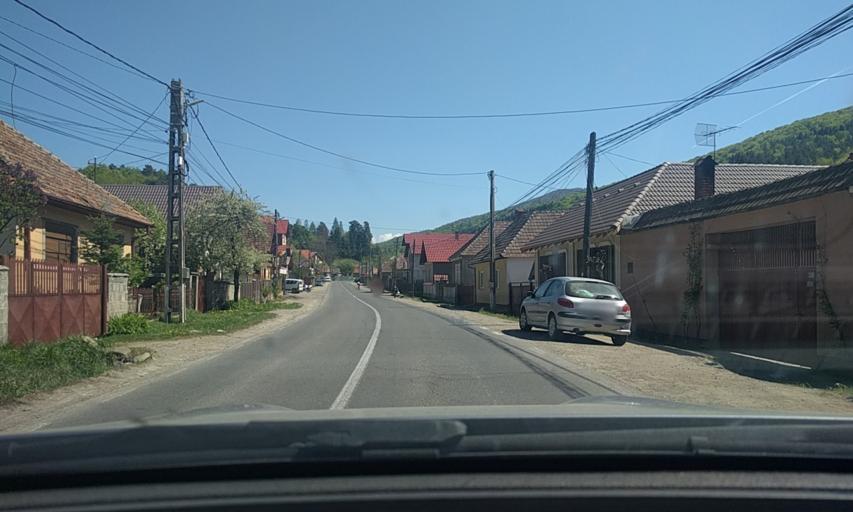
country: RO
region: Brasov
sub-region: Comuna Teliu
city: Teliu
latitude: 45.6936
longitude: 25.8728
